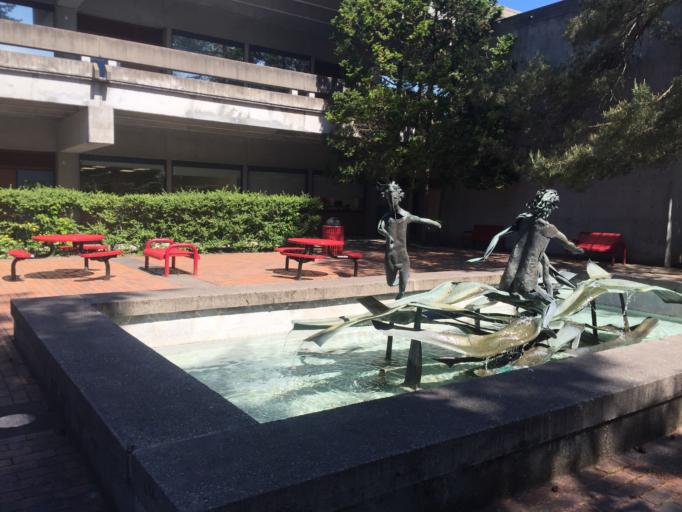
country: US
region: Oregon
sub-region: Washington County
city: Metzger
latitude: 45.4387
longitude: -122.7323
